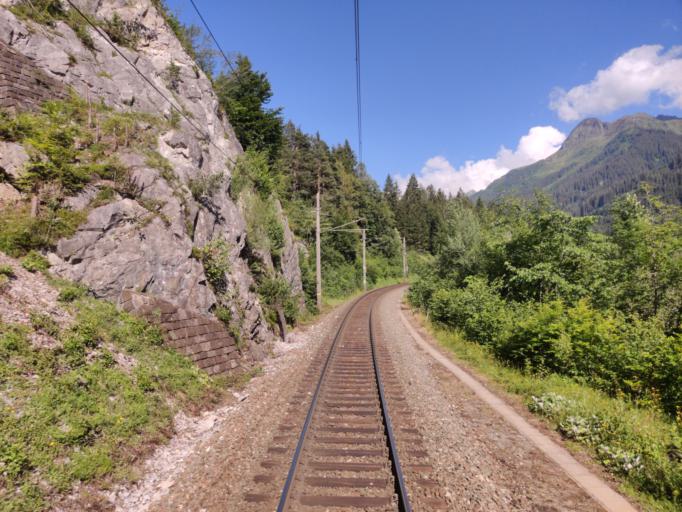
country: AT
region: Vorarlberg
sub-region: Politischer Bezirk Bludenz
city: Klosterle
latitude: 47.1331
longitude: 10.0373
